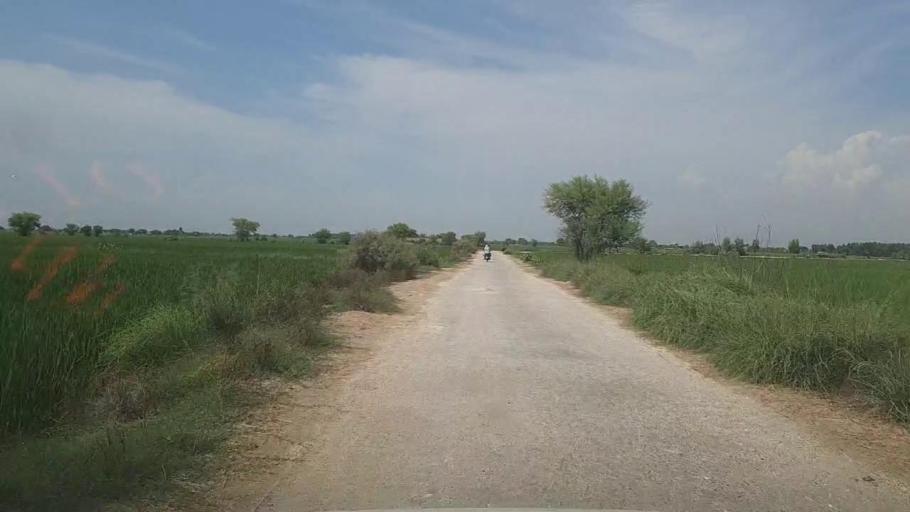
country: PK
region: Sindh
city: Kandhkot
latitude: 28.2847
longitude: 69.2376
